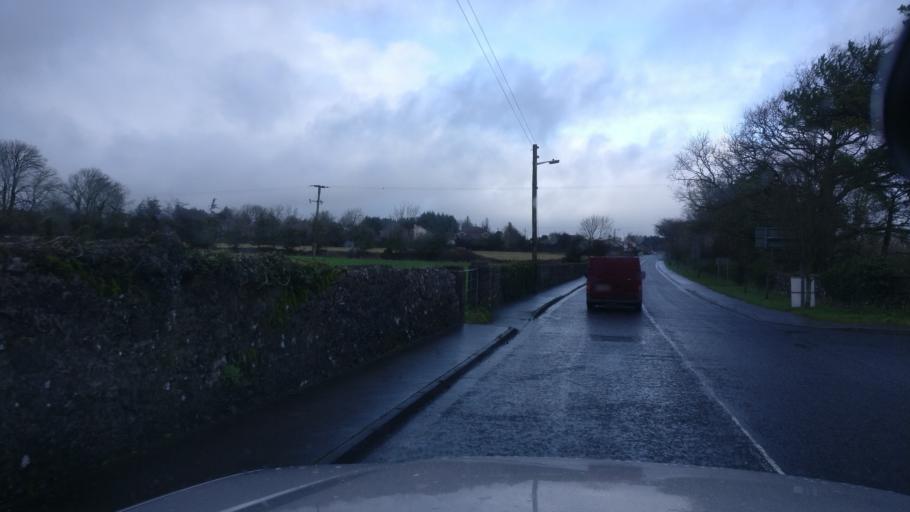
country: IE
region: Connaught
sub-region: County Galway
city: Loughrea
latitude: 53.2026
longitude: -8.5716
